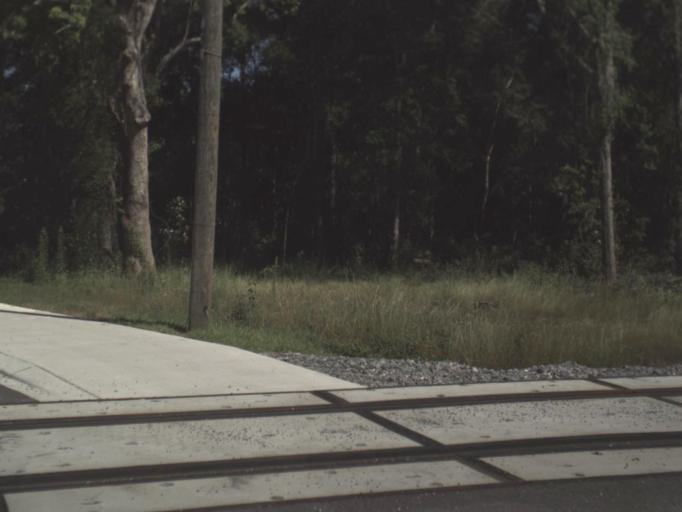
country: US
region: Florida
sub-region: Duval County
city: Baldwin
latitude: 30.3028
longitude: -81.9741
